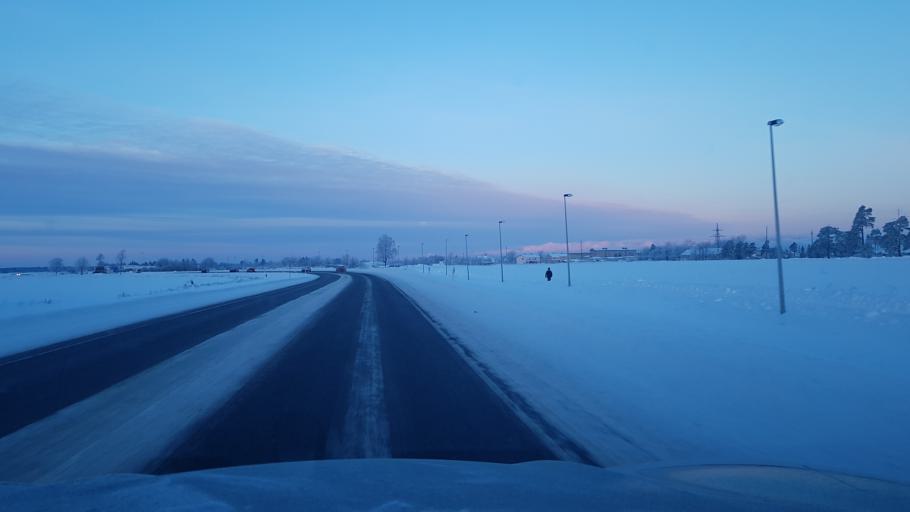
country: EE
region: Ida-Virumaa
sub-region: Narva linn
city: Narva
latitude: 59.3888
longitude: 28.1391
